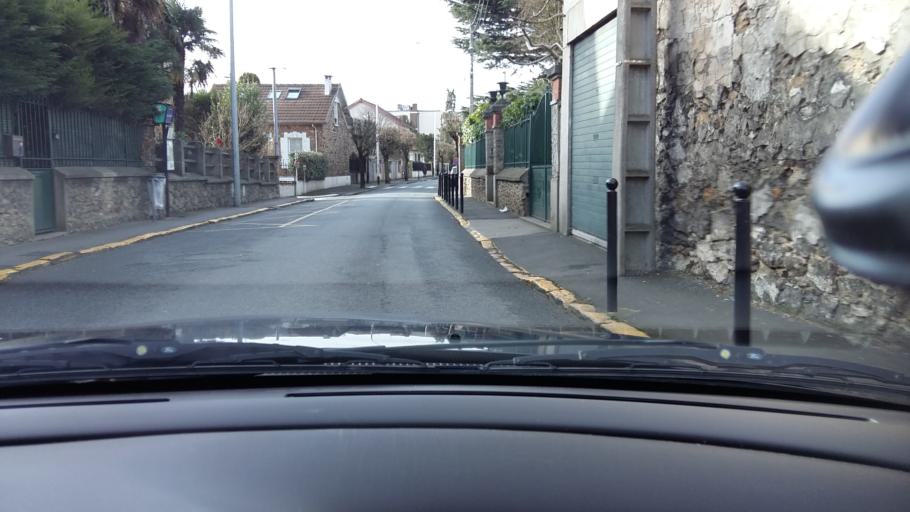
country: FR
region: Ile-de-France
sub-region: Departement de l'Essonne
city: Savigny-sur-Orge
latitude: 48.6752
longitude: 2.3471
